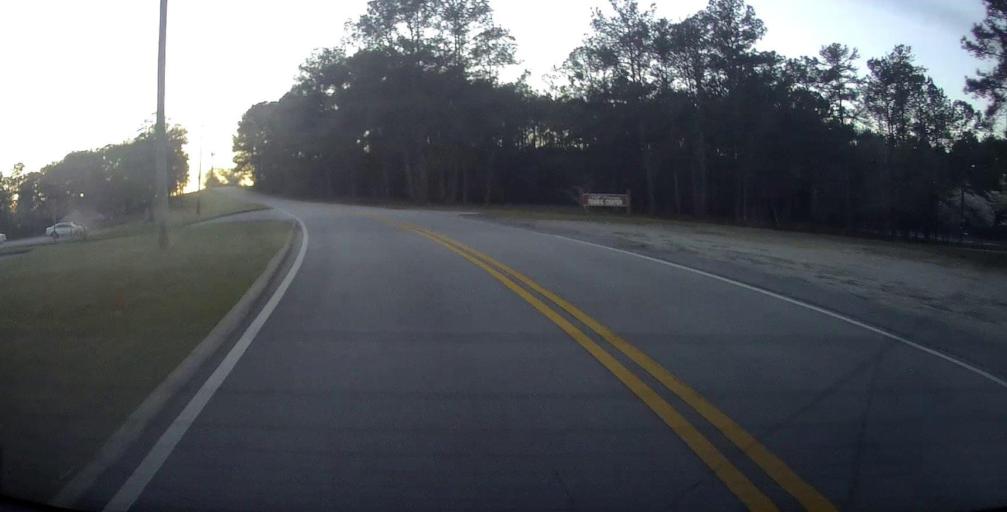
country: US
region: Alabama
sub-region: Russell County
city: Phenix City
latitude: 32.5001
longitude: -85.0076
